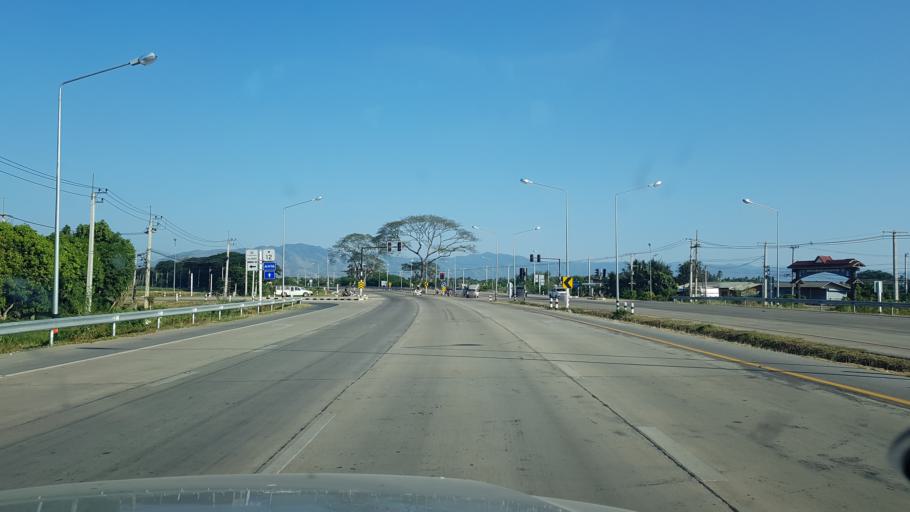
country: TH
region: Phetchabun
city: Lom Sak
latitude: 16.7272
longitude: 101.2411
